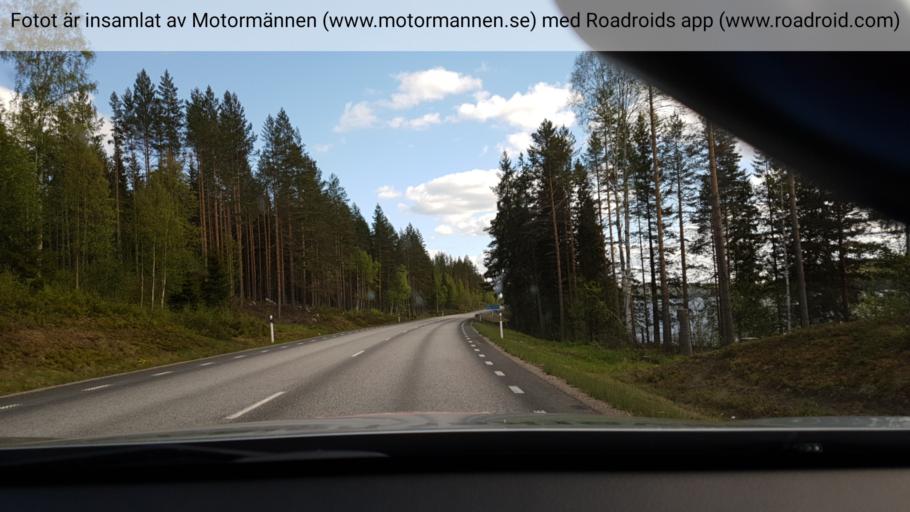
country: SE
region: Dalarna
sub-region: Faluns Kommun
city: Bjursas
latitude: 60.7767
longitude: 15.3161
